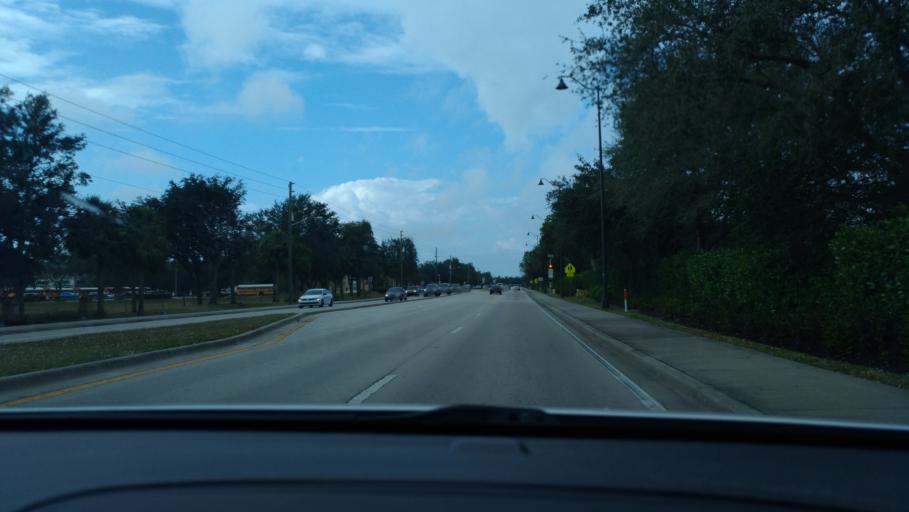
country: US
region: Florida
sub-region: Lee County
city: Bonita Springs
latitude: 26.3655
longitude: -81.7942
